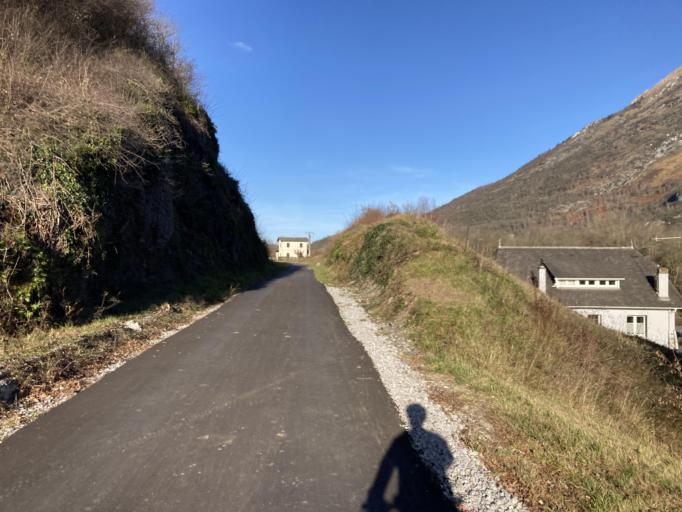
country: FR
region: Aquitaine
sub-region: Departement des Pyrenees-Atlantiques
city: Louvie-Juzon
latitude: 43.0633
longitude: -0.4254
